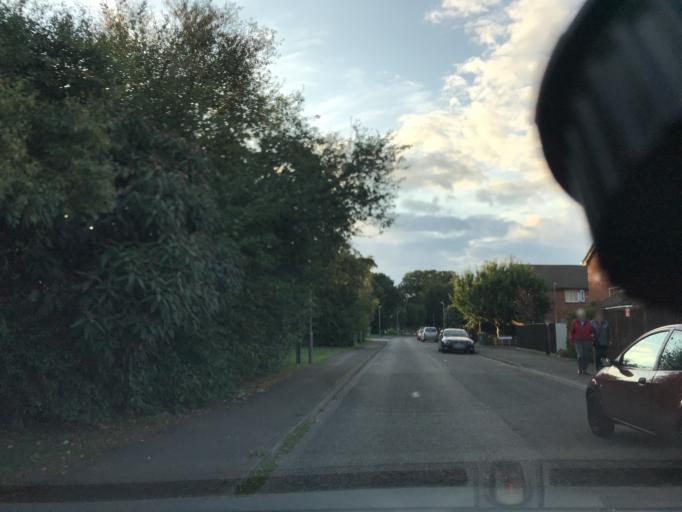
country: GB
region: England
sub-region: Buckinghamshire
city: Aylesbury
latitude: 51.8239
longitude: -0.7932
